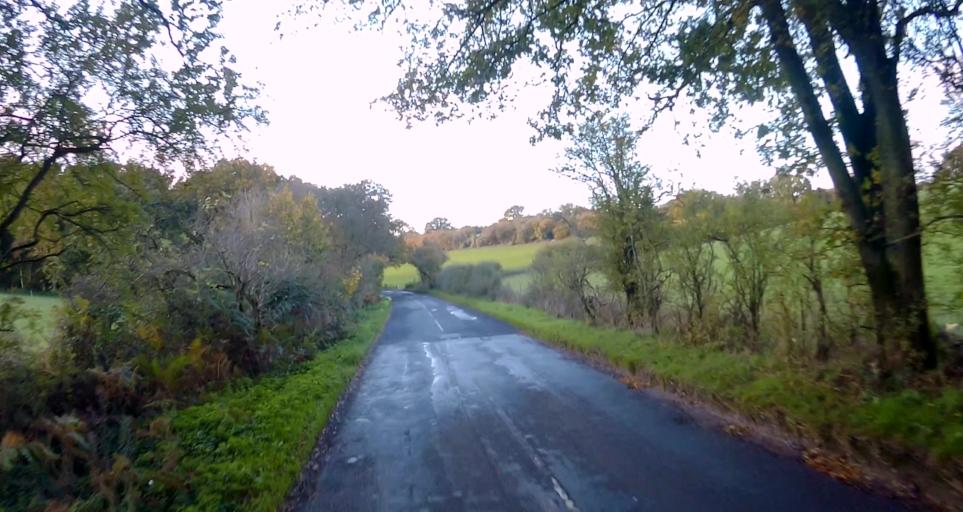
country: GB
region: England
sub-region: Hampshire
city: Basingstoke
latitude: 51.1911
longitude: -1.0805
